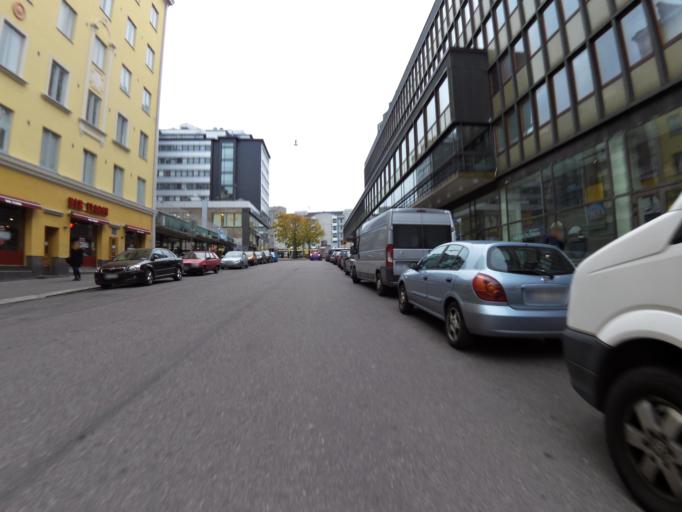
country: FI
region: Uusimaa
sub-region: Helsinki
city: Helsinki
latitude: 60.1874
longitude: 24.9649
